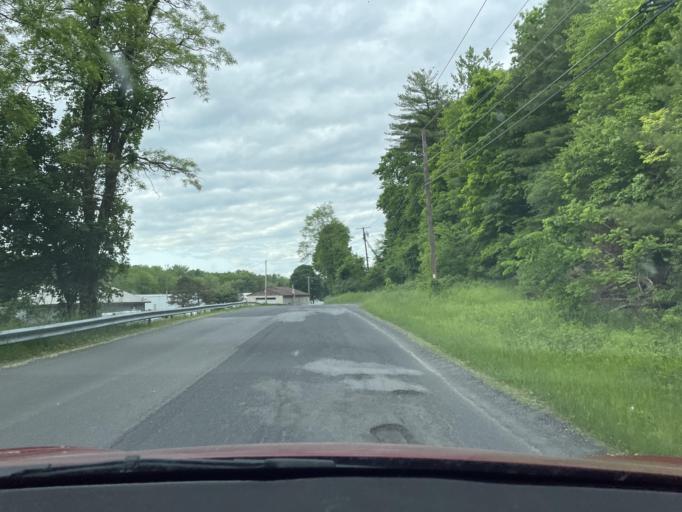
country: US
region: New York
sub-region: Ulster County
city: Saugerties
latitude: 42.0839
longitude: -73.9596
